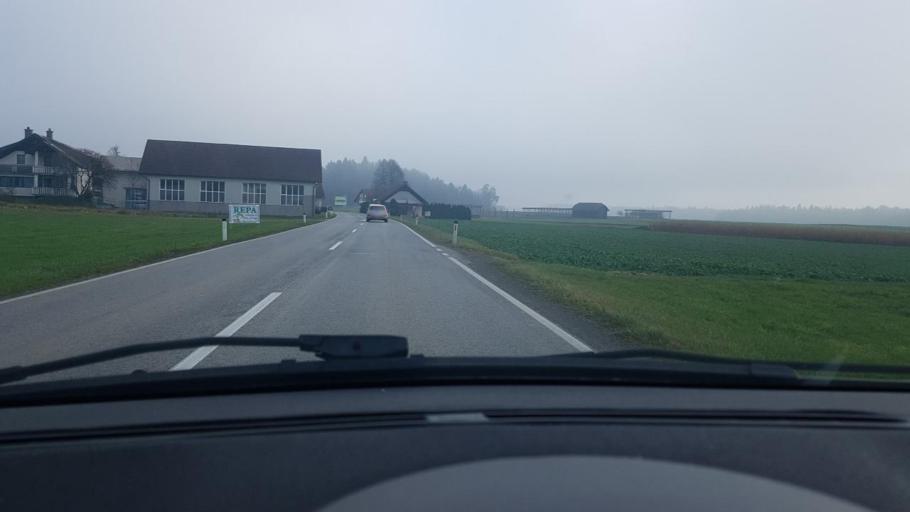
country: SI
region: Vodice
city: Vodice
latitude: 46.2168
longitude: 14.5029
